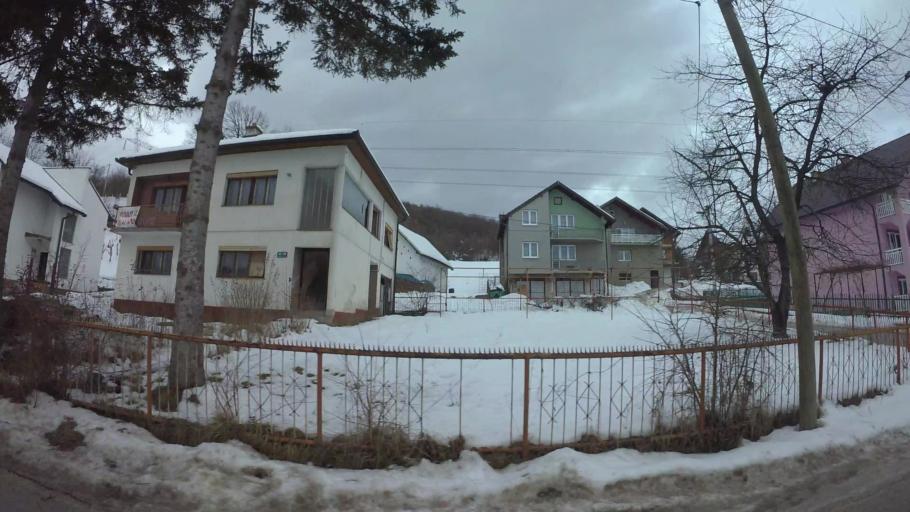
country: BA
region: Federation of Bosnia and Herzegovina
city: Vogosca
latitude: 43.8855
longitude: 18.3061
